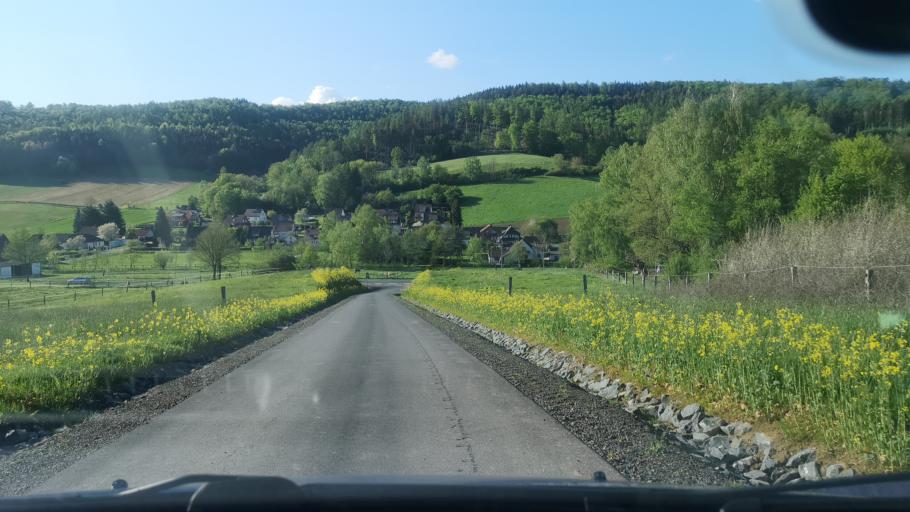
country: DE
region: Lower Saxony
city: Uslar
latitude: 51.6611
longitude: 9.7203
